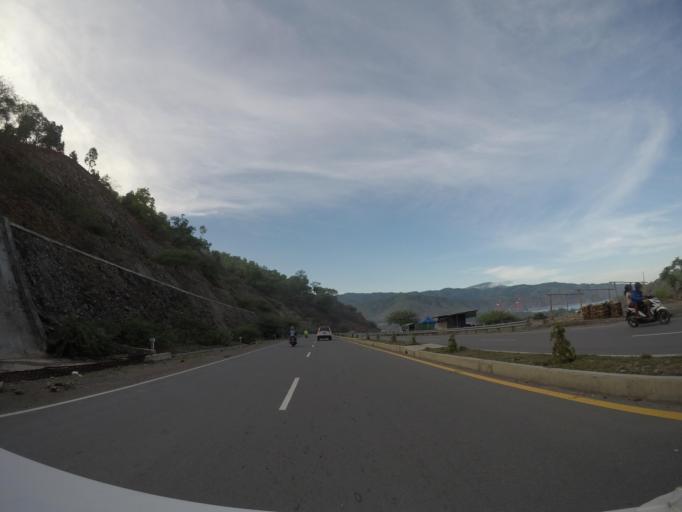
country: TL
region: Dili
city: Dili
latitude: -8.5623
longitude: 125.4926
